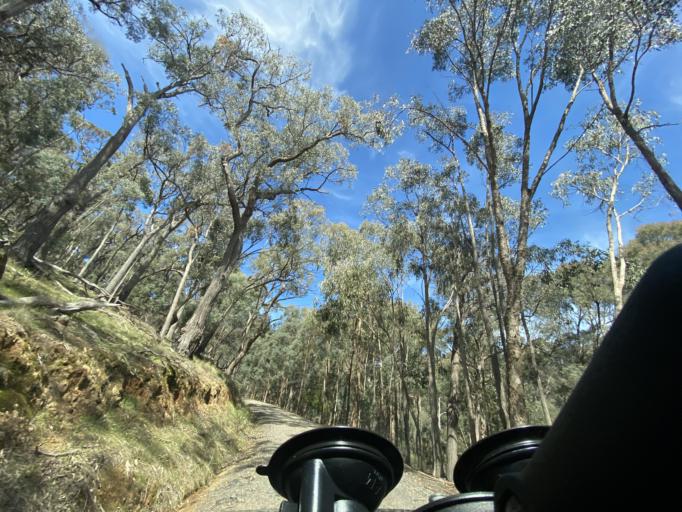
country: AU
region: Victoria
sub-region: Mansfield
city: Mansfield
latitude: -36.8112
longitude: 146.1023
